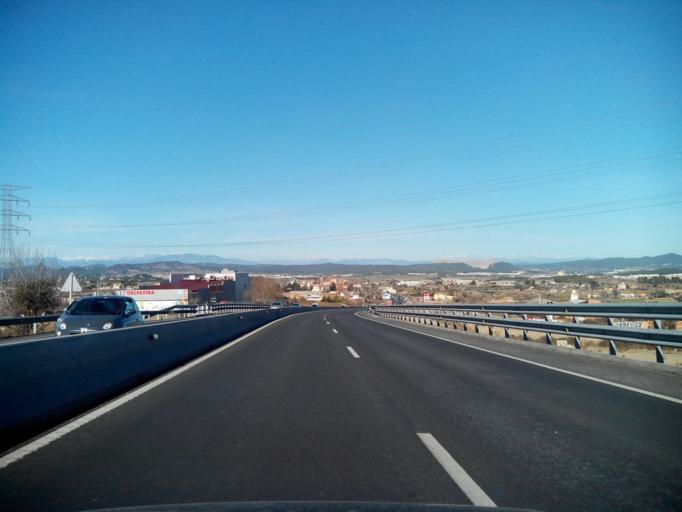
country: ES
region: Catalonia
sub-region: Provincia de Barcelona
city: Manresa
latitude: 41.7202
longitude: 1.8513
